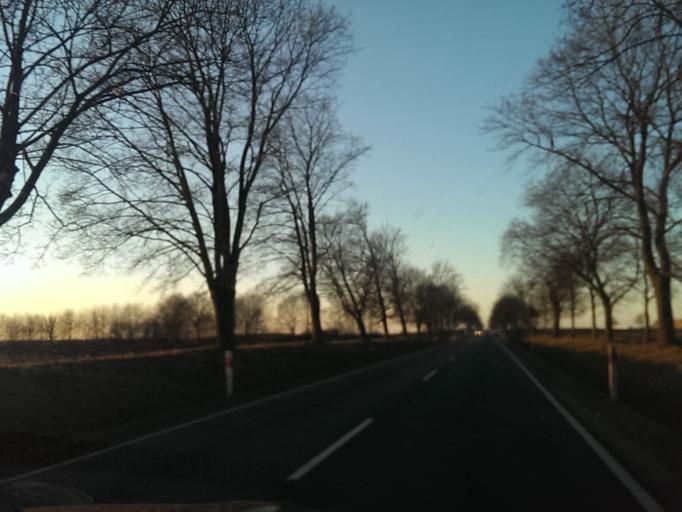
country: PL
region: Kujawsko-Pomorskie
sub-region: Powiat nakielski
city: Slesin
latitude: 53.0813
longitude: 17.6825
